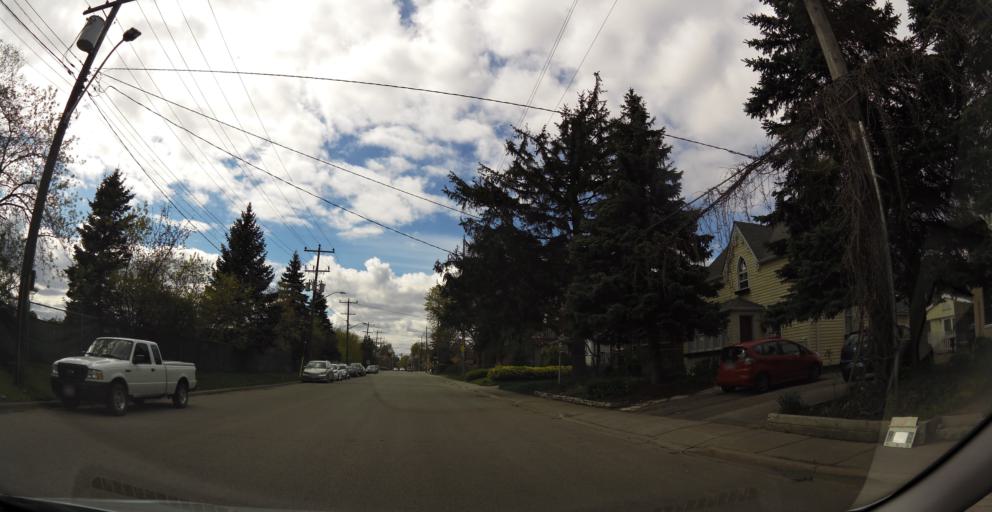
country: CA
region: Ontario
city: Mississauga
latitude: 43.5469
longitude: -79.5875
